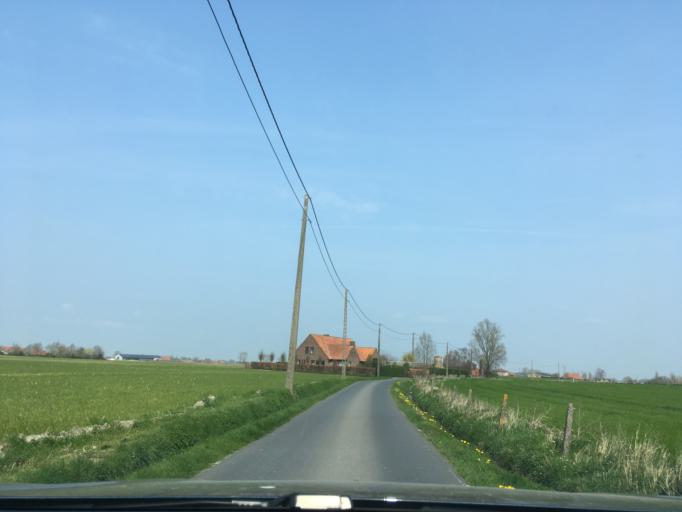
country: BE
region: Flanders
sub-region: Provincie West-Vlaanderen
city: Ardooie
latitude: 51.0119
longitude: 3.1869
